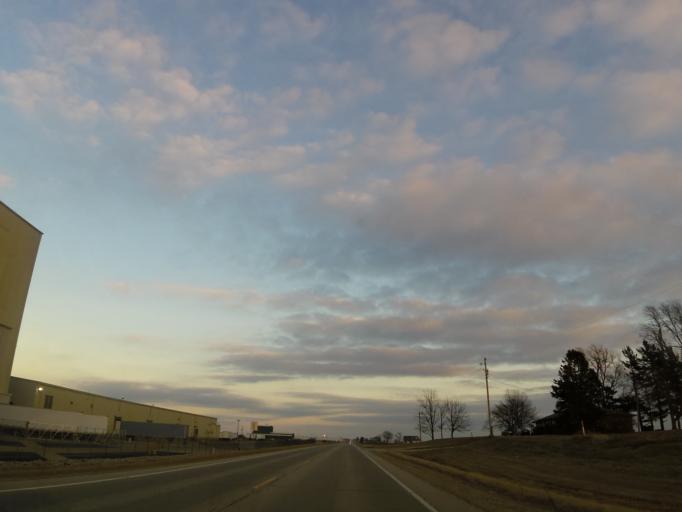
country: US
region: Illinois
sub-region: Woodford County
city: El Paso
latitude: 40.7377
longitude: -88.9970
